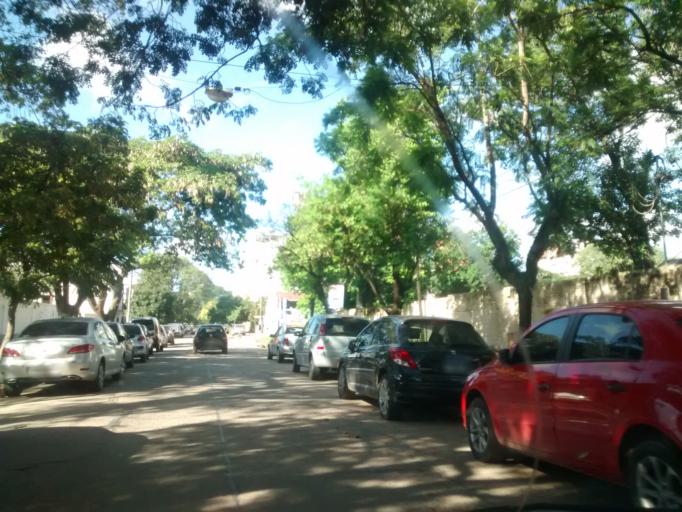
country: AR
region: Chaco
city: Resistencia
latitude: -27.4569
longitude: -58.9808
